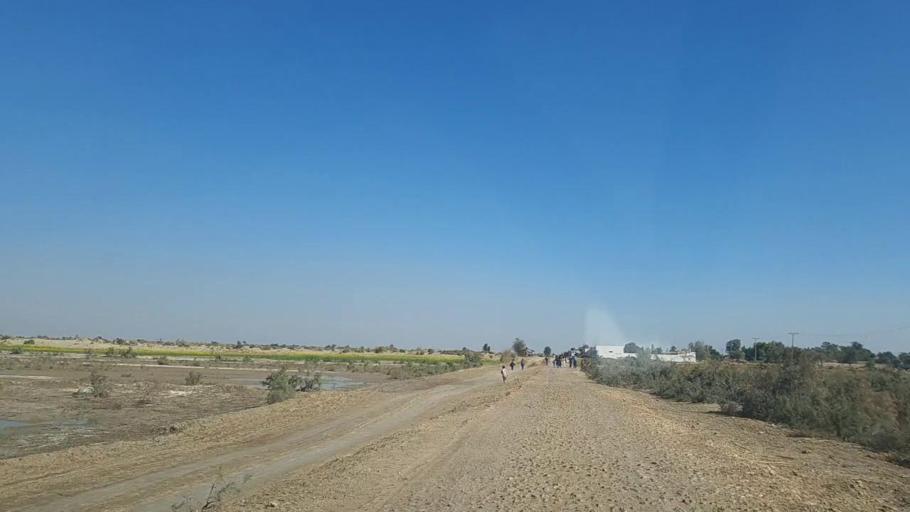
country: PK
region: Sindh
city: Sanghar
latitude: 26.2091
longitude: 68.8899
